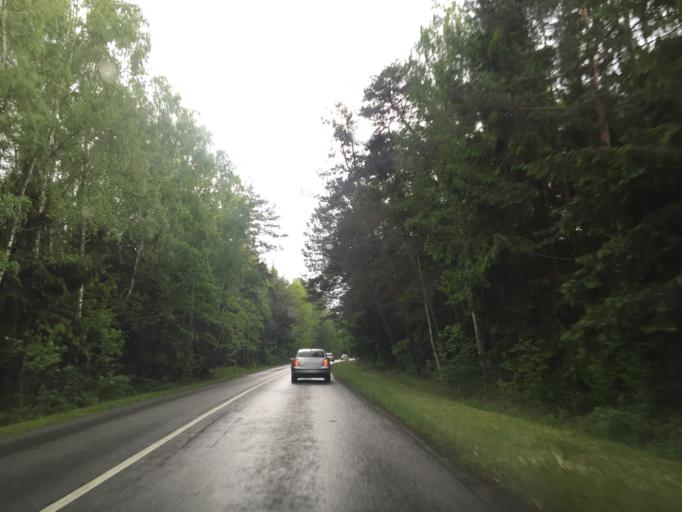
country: LT
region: Klaipedos apskritis
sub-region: Klaipeda
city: Klaipeda
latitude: 55.7440
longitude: 21.0944
